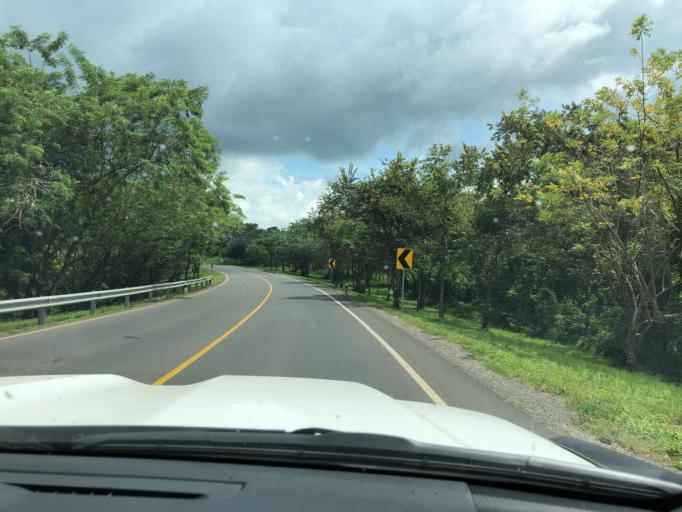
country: NI
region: Chontales
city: Villa Sandino
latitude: 12.0553
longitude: -85.0379
